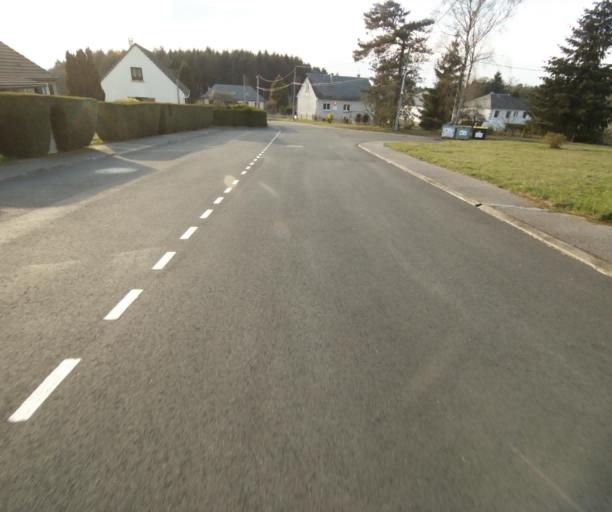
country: FR
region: Limousin
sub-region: Departement de la Correze
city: Correze
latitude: 45.3751
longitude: 1.8663
